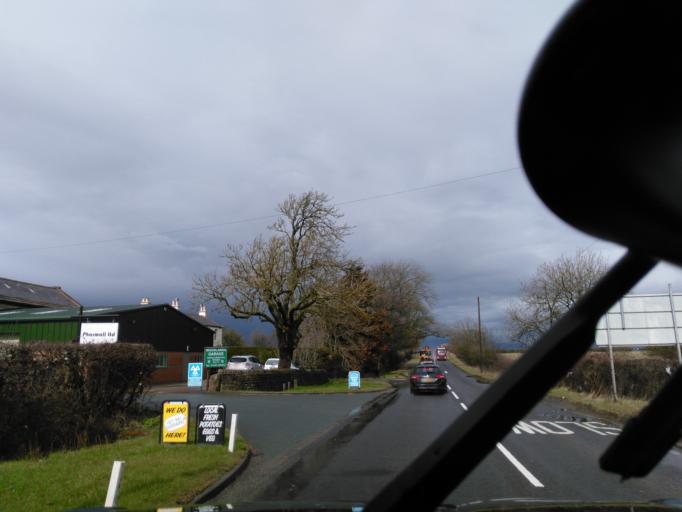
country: GB
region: England
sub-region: North Yorkshire
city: Harrogate
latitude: 54.0089
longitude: -1.5775
